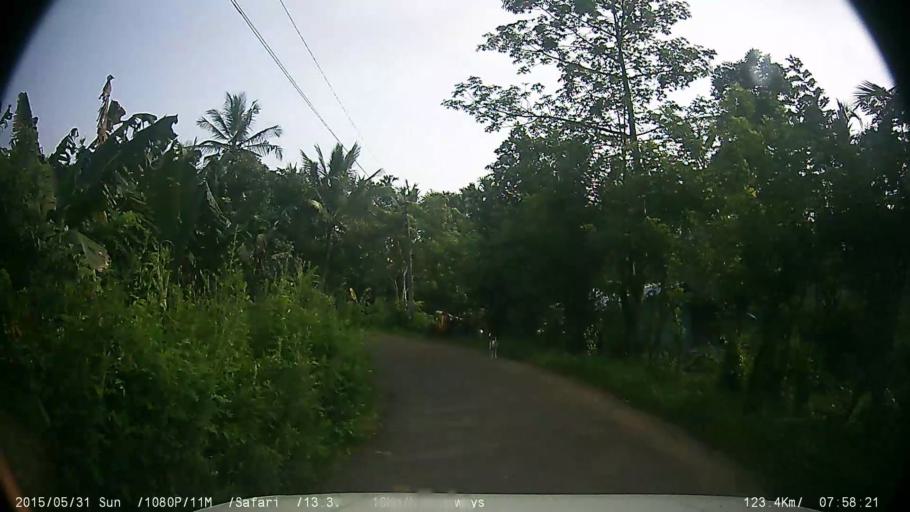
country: IN
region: Kerala
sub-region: Wayanad
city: Kalpetta
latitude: 11.6342
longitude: 76.0621
